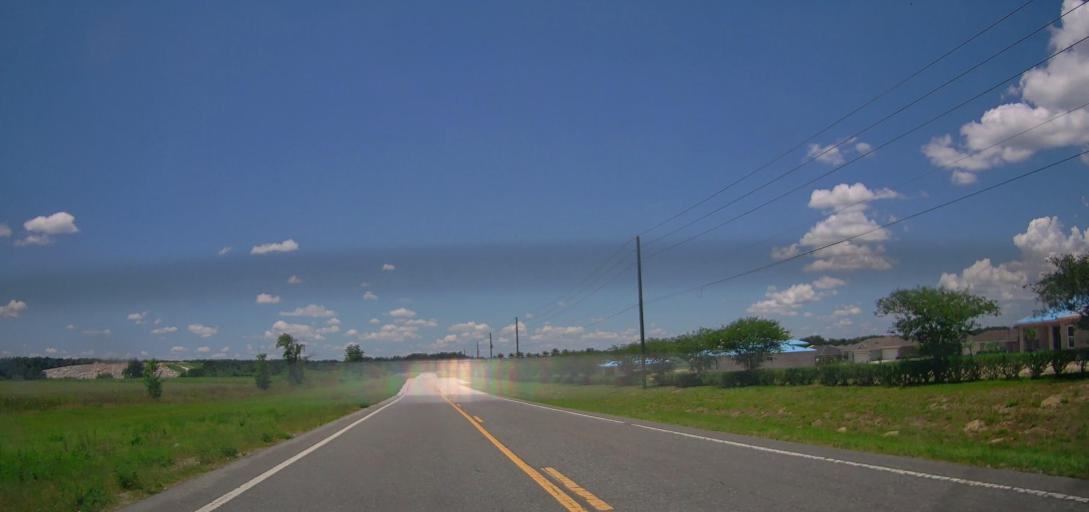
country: US
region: Florida
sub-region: Marion County
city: Belleview
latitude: 29.0864
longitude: -82.0611
